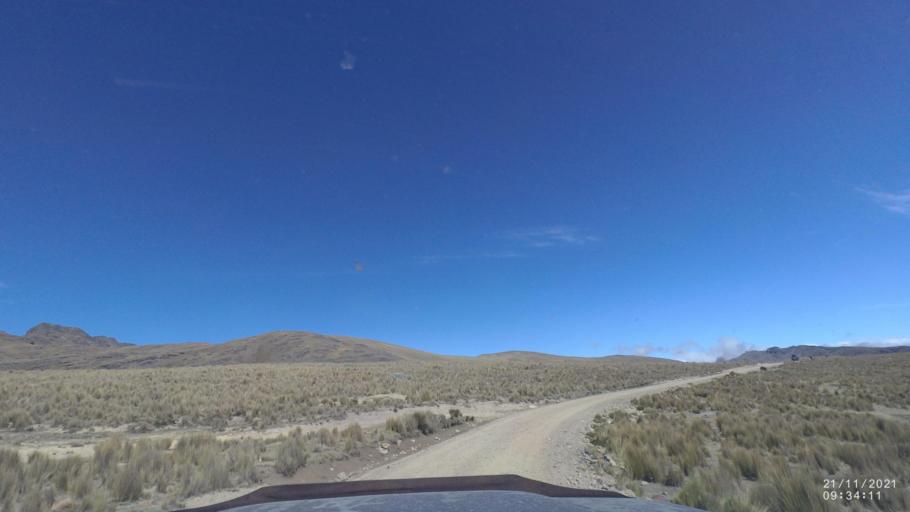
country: BO
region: Cochabamba
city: Cochabamba
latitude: -17.0580
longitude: -66.2594
